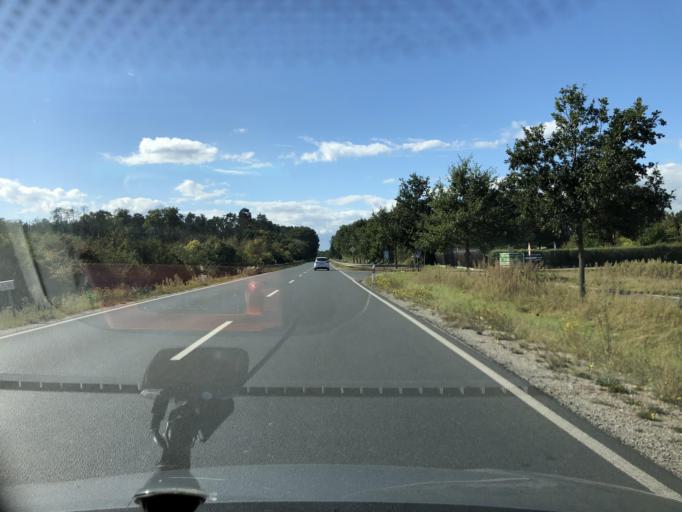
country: DE
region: Bavaria
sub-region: Regierungsbezirk Mittelfranken
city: Zirndorf
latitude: 49.4307
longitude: 10.9295
